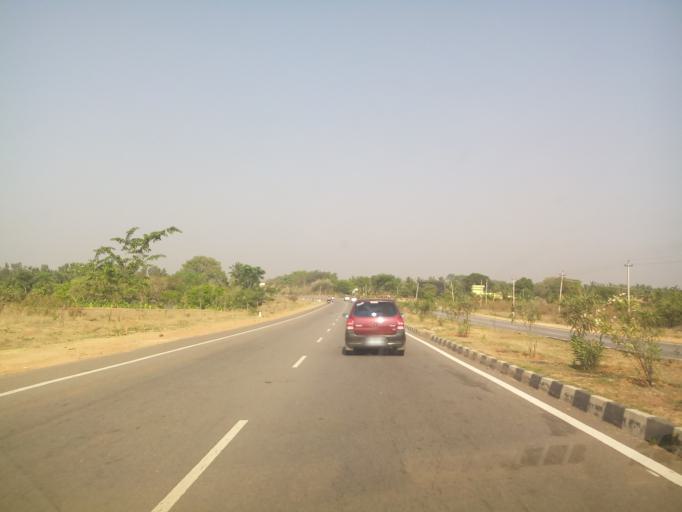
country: IN
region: Karnataka
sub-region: Tumkur
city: Kunigal
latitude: 13.0418
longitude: 77.1176
